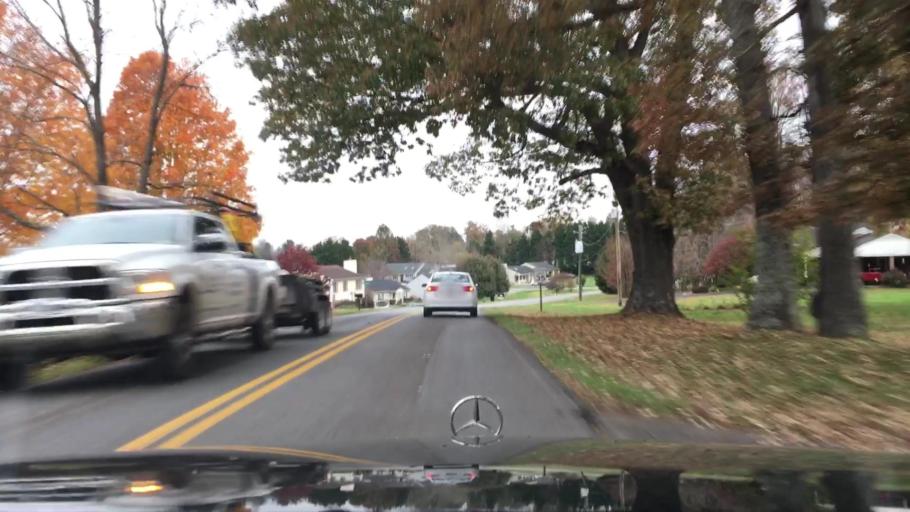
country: US
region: Virginia
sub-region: Campbell County
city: Timberlake
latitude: 37.2968
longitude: -79.2820
